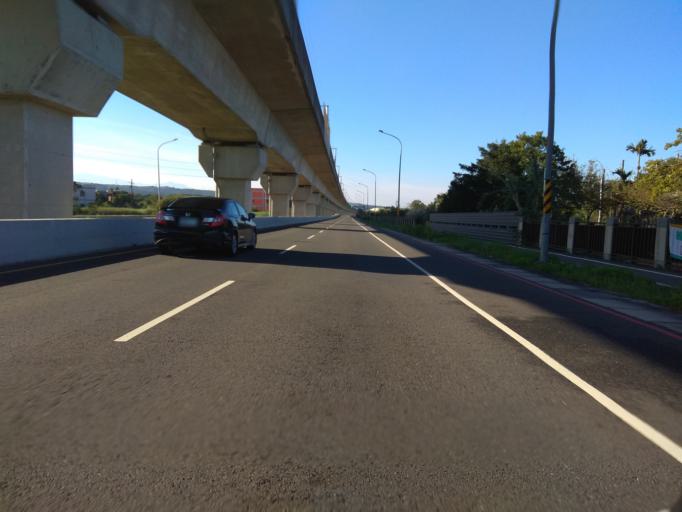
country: TW
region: Taiwan
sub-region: Hsinchu
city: Zhubei
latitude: 24.9098
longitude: 121.0875
